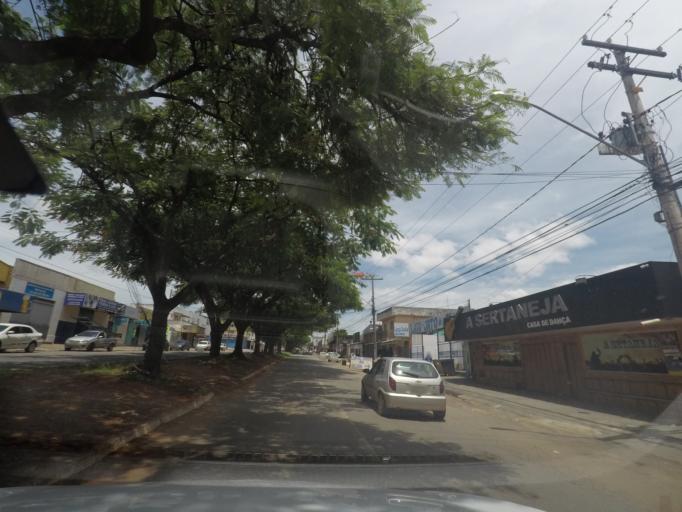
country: BR
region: Goias
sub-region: Goiania
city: Goiania
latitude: -16.6646
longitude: -49.2151
